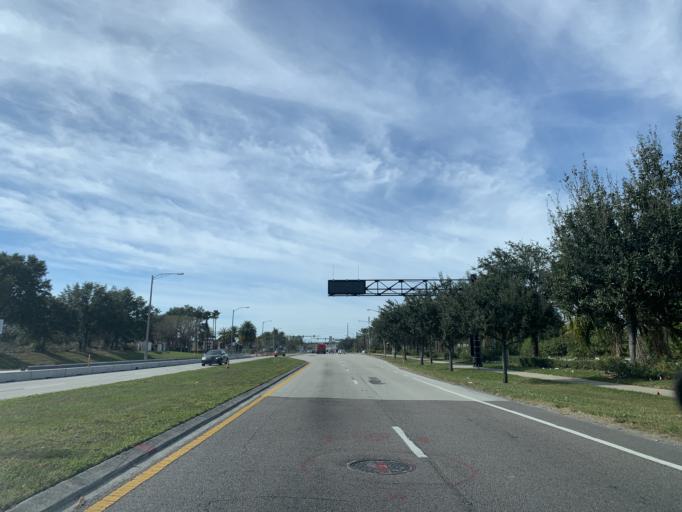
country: US
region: Florida
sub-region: Orange County
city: Tangelo Park
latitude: 28.4721
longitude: -81.4480
